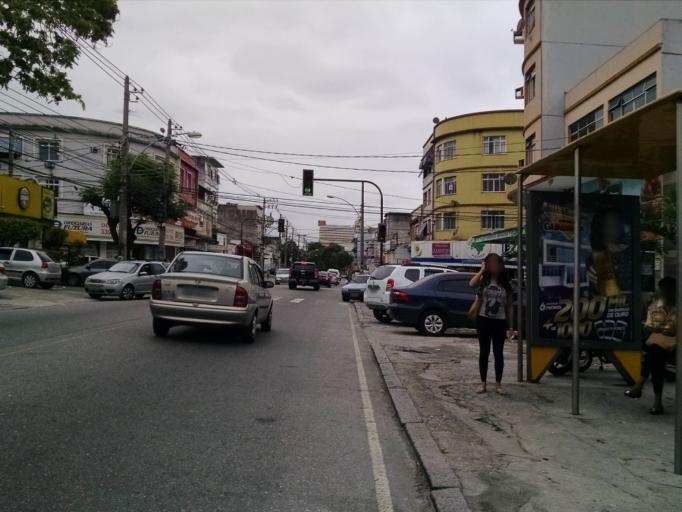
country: BR
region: Rio de Janeiro
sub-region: Duque De Caxias
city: Duque de Caxias
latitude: -22.8315
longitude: -43.3190
